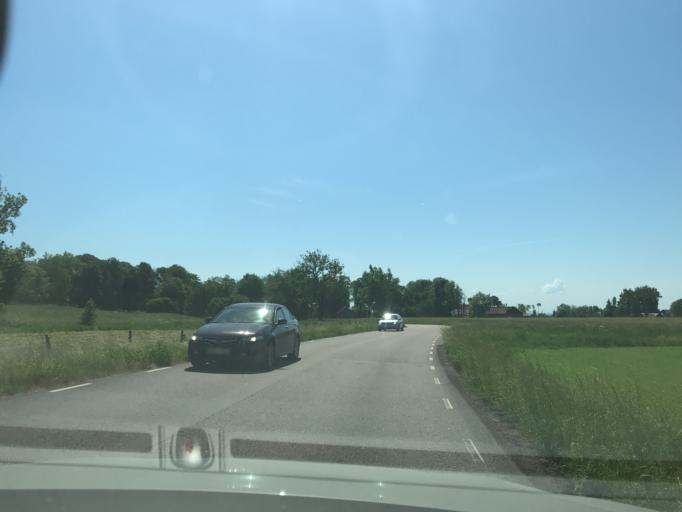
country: SE
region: Vaestra Goetaland
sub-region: Gotene Kommun
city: Kallby
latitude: 58.5848
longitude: 13.3755
